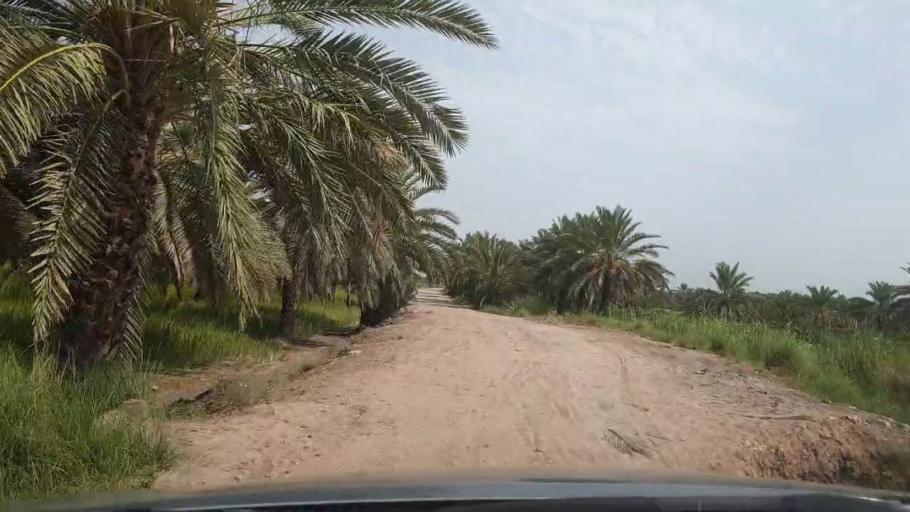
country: PK
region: Sindh
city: Rohri
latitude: 27.6795
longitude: 69.0355
